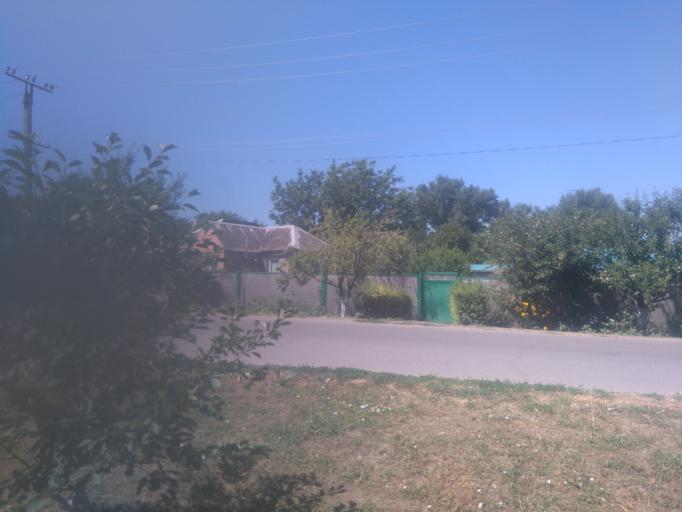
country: RU
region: Krasnodarskiy
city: Fastovetskaya
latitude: 45.9132
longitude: 40.1544
